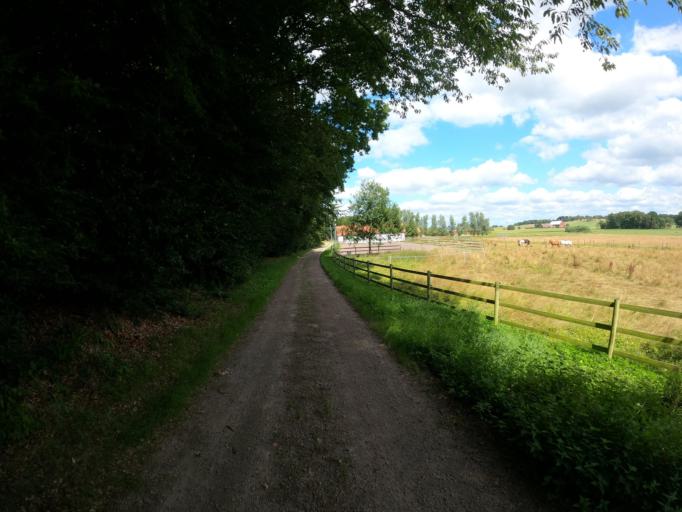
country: SE
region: Skane
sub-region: Lunds Kommun
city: Veberod
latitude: 55.5956
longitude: 13.4831
